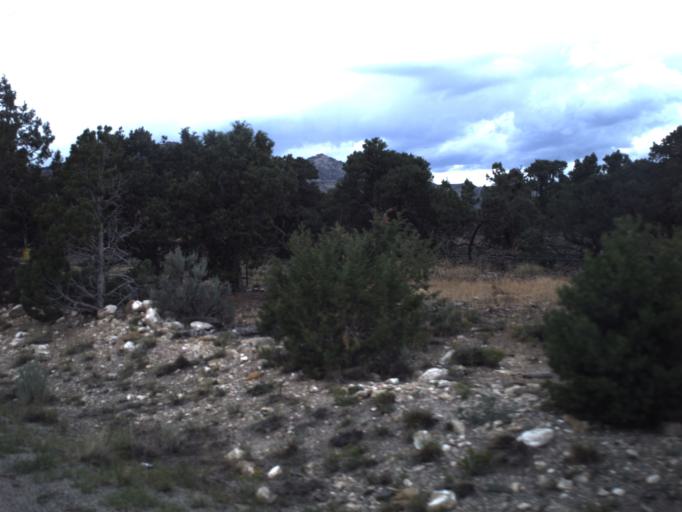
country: US
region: Utah
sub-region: Emery County
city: Huntington
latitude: 39.4842
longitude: -110.9697
